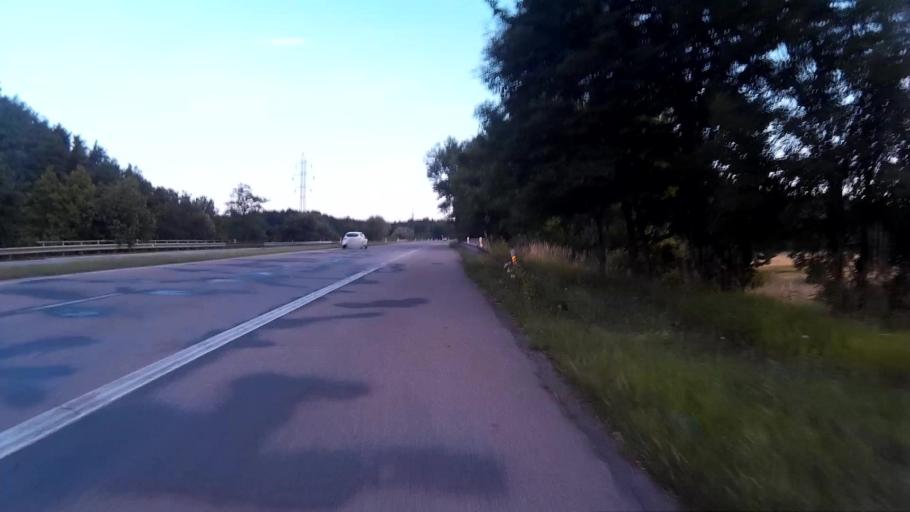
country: CZ
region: South Moravian
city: Troubsko
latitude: 49.2047
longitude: 16.5192
